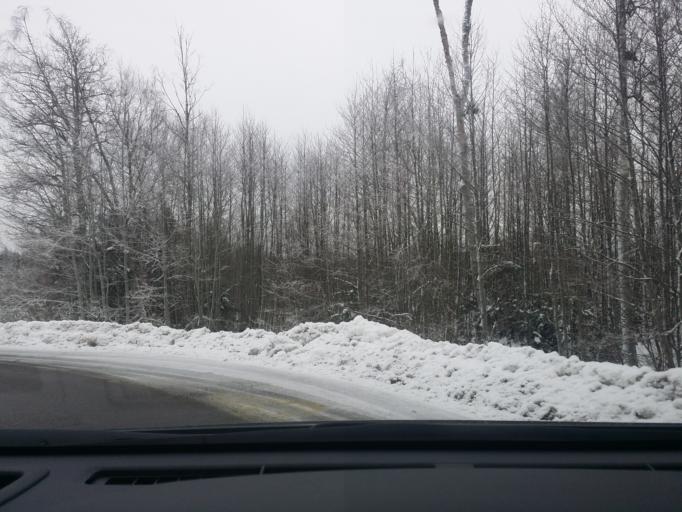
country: SE
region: Vaestra Goetaland
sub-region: Gullspangs Kommun
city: Anderstorp
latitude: 58.9014
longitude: 14.3405
